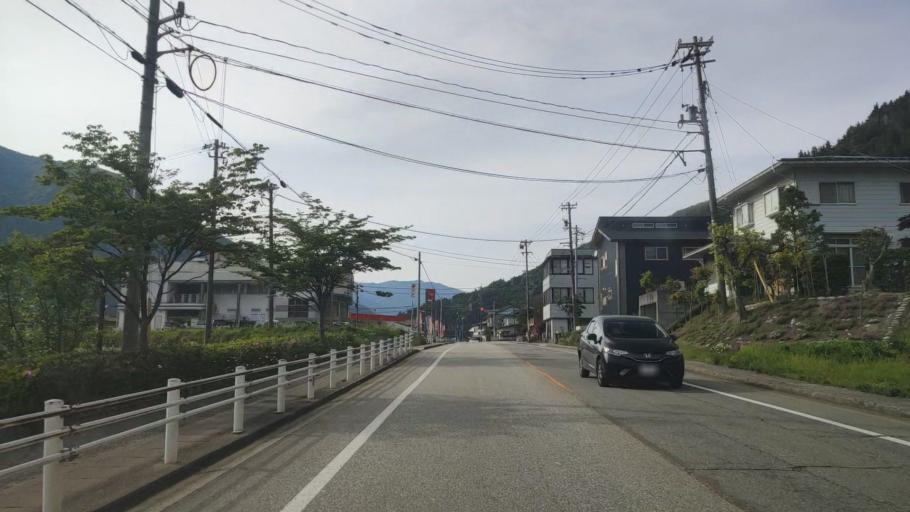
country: JP
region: Gifu
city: Takayama
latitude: 36.3263
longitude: 137.3082
